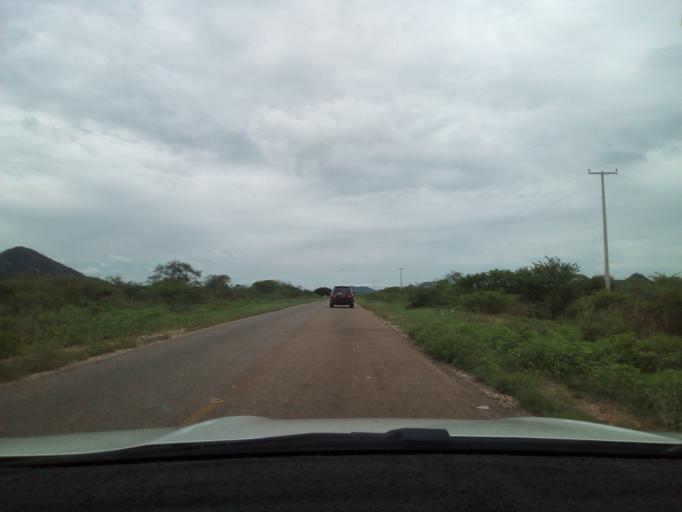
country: BR
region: Rio Grande do Norte
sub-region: Patu
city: Patu
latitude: -6.1035
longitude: -37.7286
